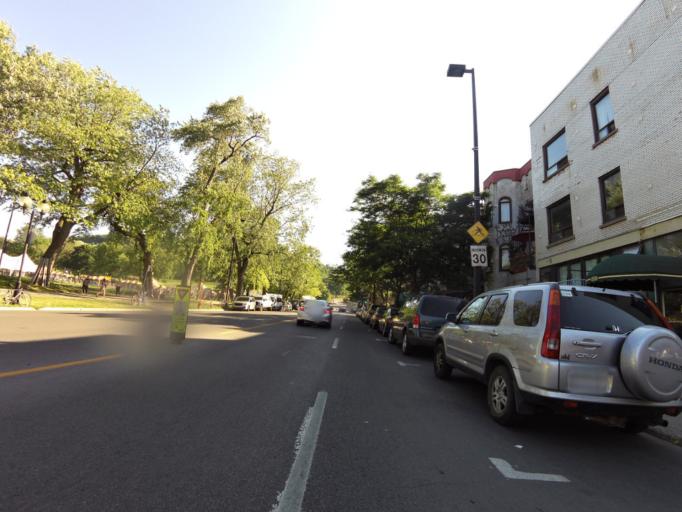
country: CA
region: Quebec
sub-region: Montreal
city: Montreal
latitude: 45.5182
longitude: -73.5882
